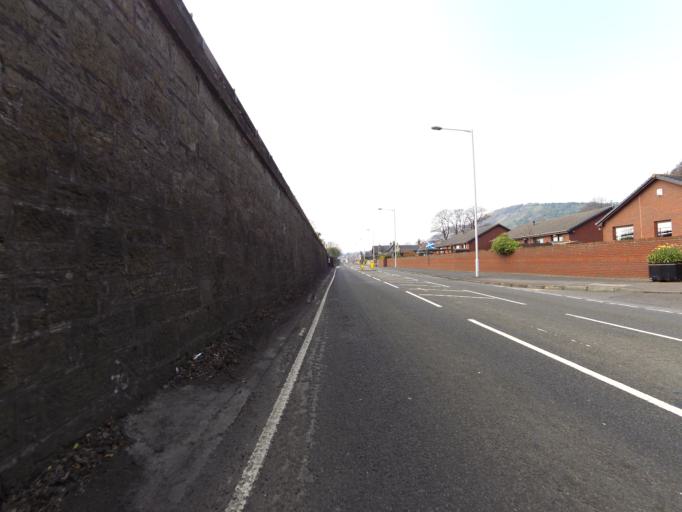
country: GB
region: Scotland
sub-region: Fife
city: Burntisland
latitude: 56.0645
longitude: -3.2104
